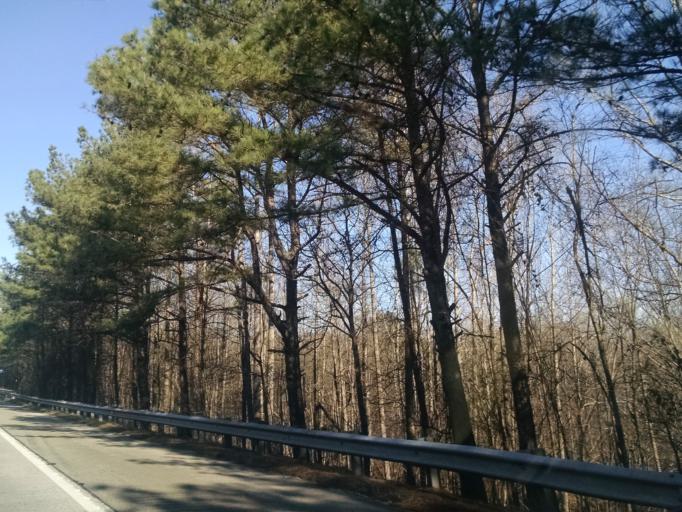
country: US
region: Georgia
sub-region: Gwinnett County
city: Sugar Hill
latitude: 34.0635
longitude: -84.0148
